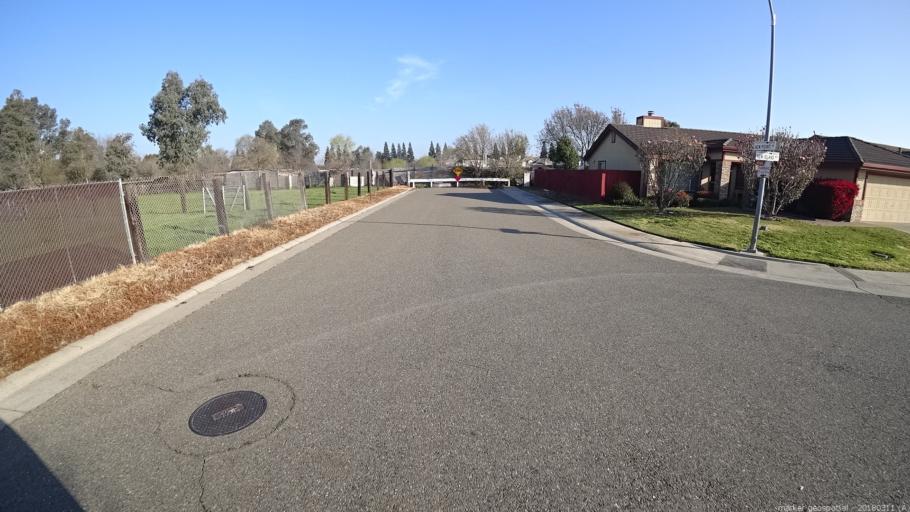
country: US
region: California
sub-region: Sacramento County
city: Vineyard
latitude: 38.4576
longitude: -121.3881
